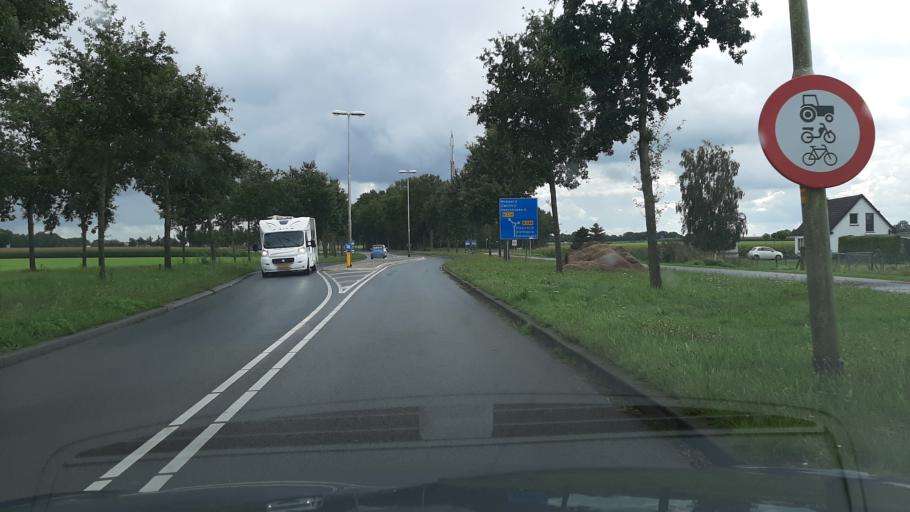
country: NL
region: Overijssel
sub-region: Gemeente Steenwijkerland
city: Tuk
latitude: 52.8063
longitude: 6.0819
